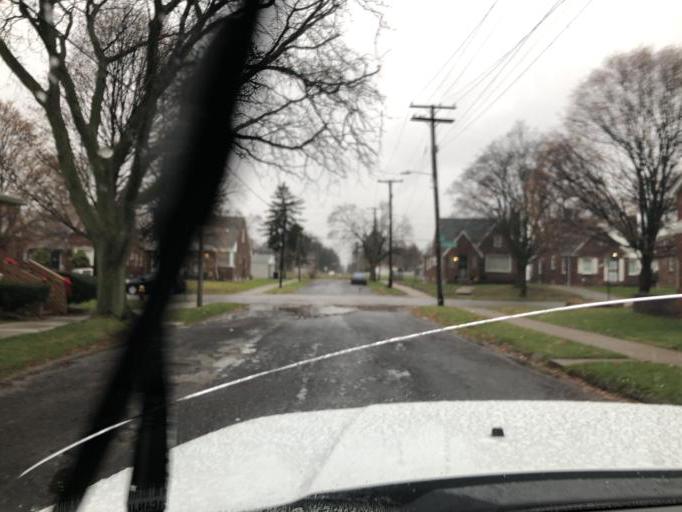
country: US
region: Michigan
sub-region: Oakland County
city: Oak Park
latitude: 42.4102
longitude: -83.2171
